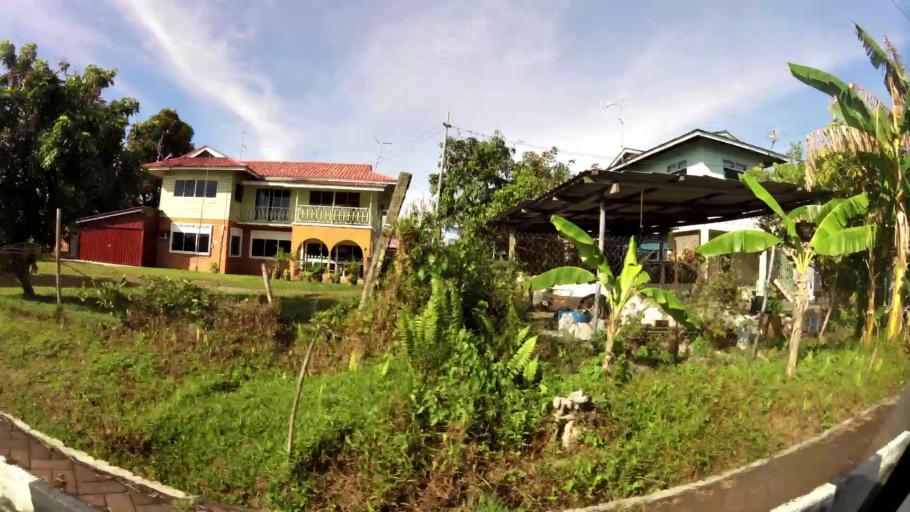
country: BN
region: Belait
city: Kuala Belait
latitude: 4.5828
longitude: 114.1895
